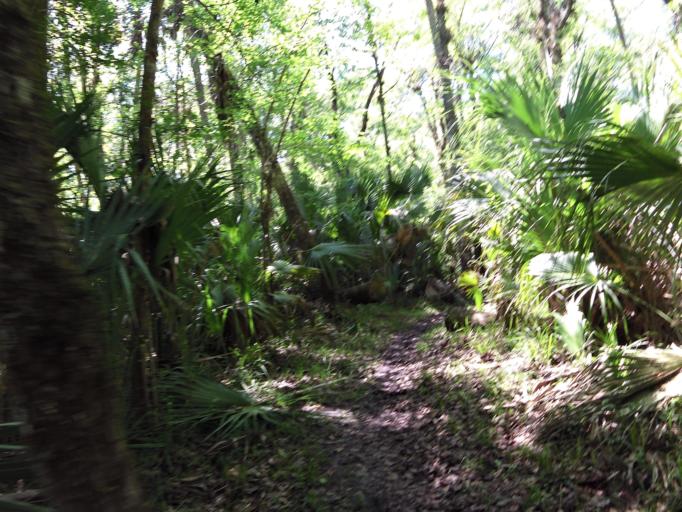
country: US
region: Florida
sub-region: Putnam County
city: Palatka
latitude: 29.6776
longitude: -81.7520
